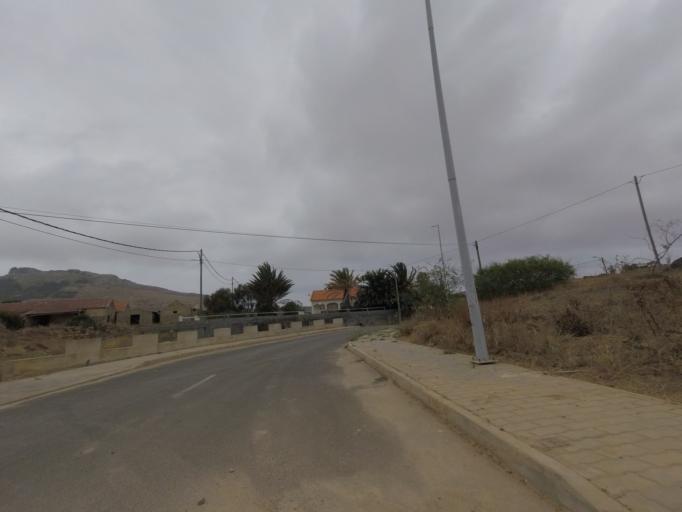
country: PT
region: Madeira
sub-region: Porto Santo
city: Vila de Porto Santo
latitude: 33.0483
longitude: -16.3547
